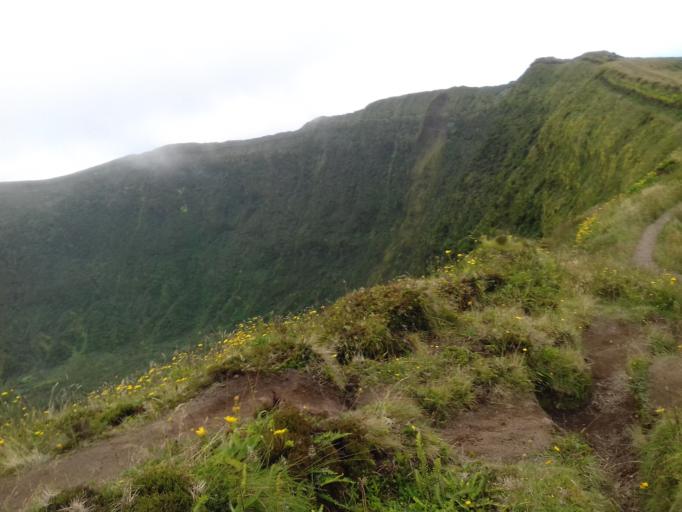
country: PT
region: Azores
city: Ribeira Grande
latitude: 38.5913
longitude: -28.7061
